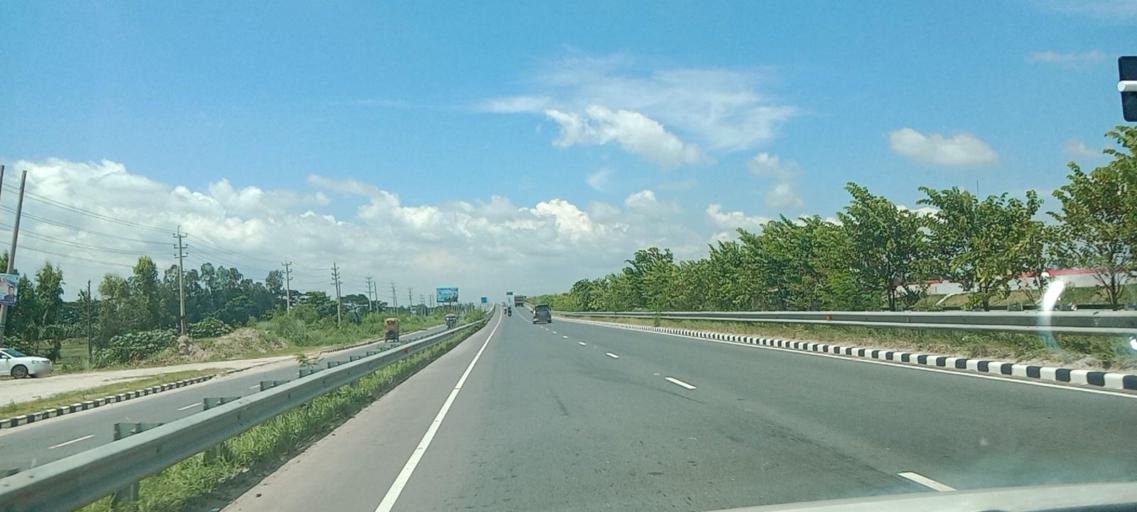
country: BD
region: Dhaka
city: Dohar
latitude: 23.5017
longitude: 90.2730
